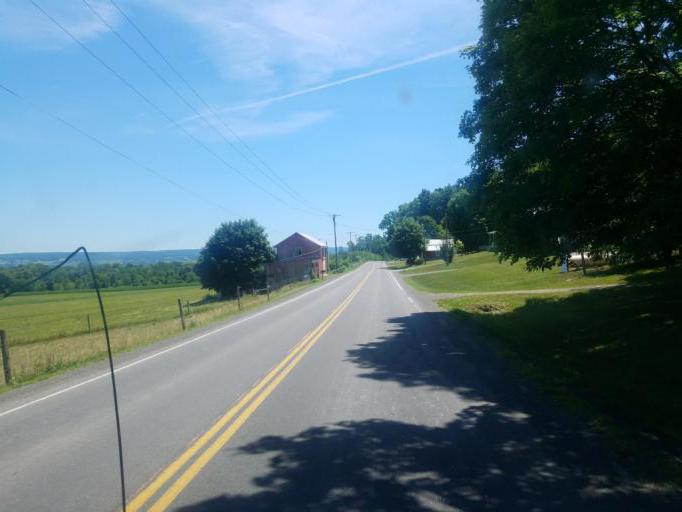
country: US
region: New York
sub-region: Yates County
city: Dundee
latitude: 42.5969
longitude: -76.9632
